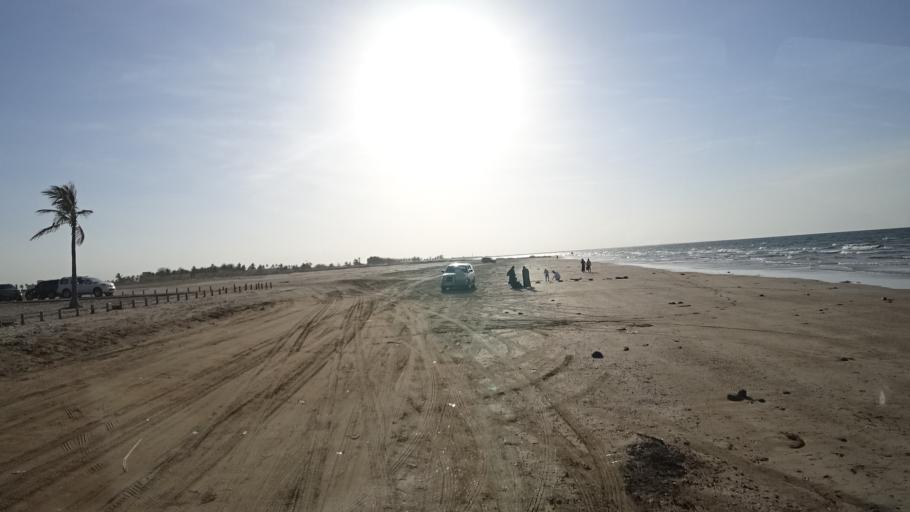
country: OM
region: Al Batinah
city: Barka'
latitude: 23.7811
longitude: 57.7877
